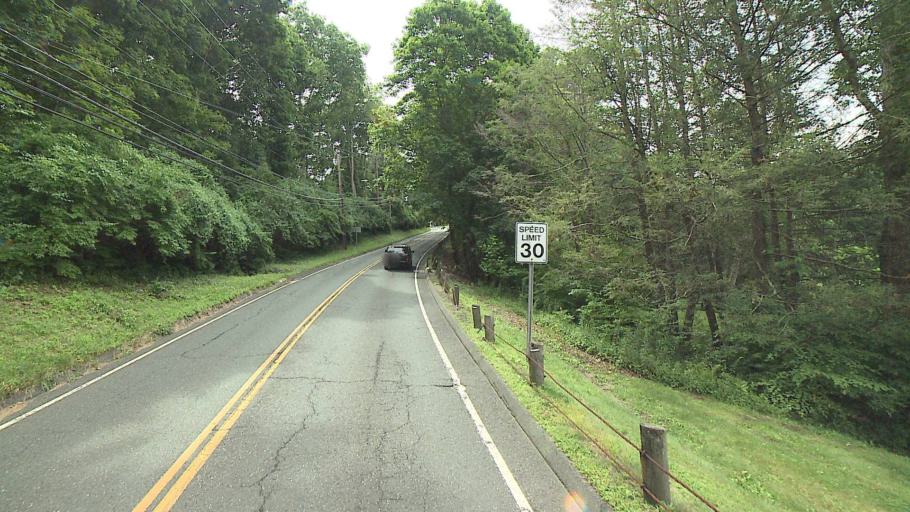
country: US
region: Connecticut
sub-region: Litchfield County
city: New Preston
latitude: 41.6331
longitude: -73.3145
